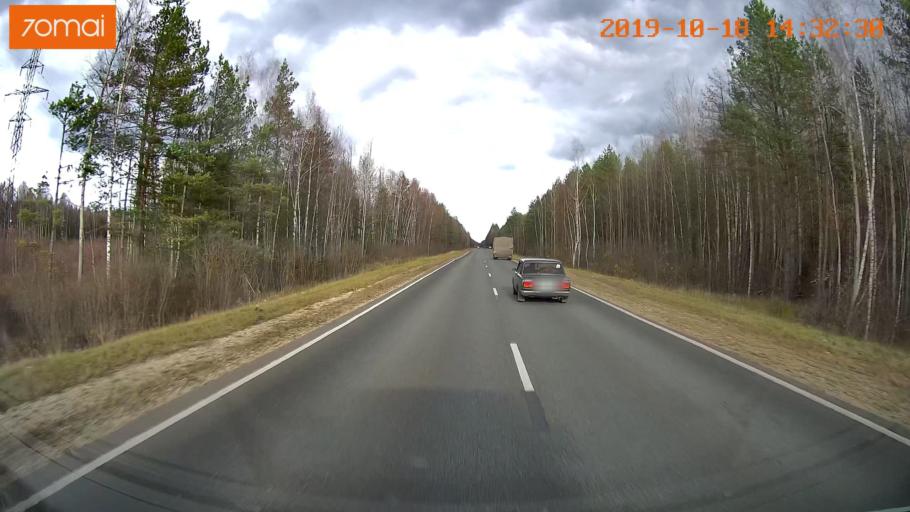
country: RU
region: Rjazan
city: Tuma
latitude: 55.1920
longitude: 40.5810
